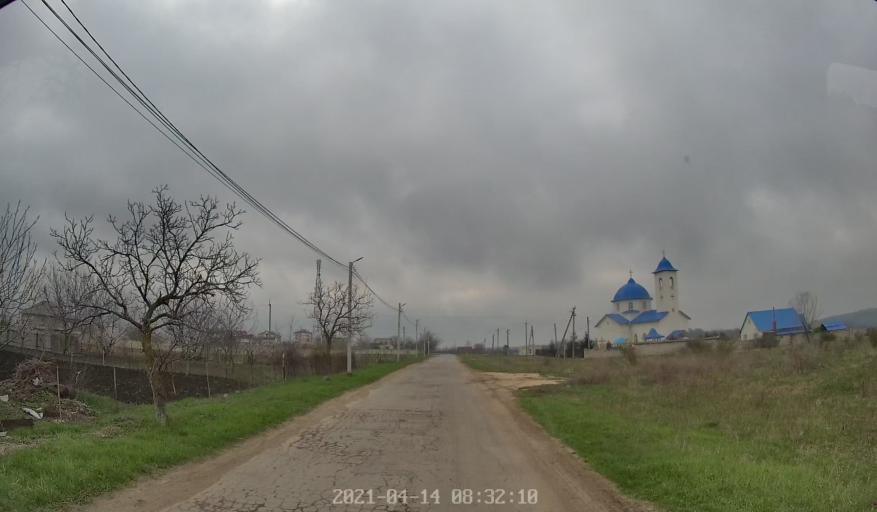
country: MD
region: Chisinau
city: Stauceni
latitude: 47.0599
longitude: 28.9388
